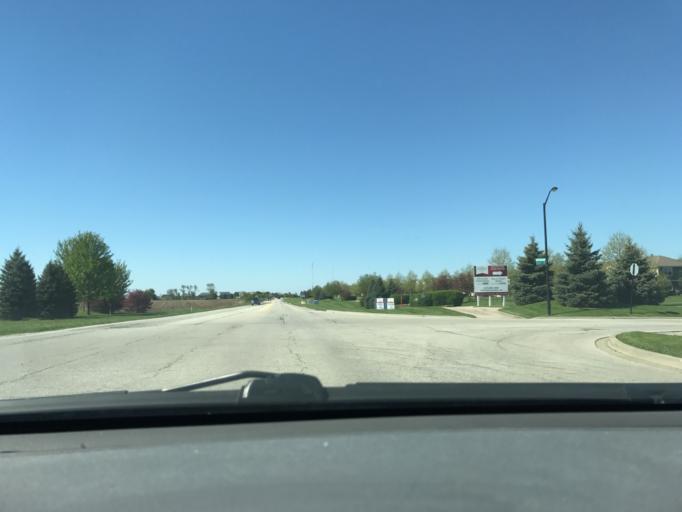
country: US
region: Illinois
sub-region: Kane County
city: Pingree Grove
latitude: 42.0377
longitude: -88.3651
